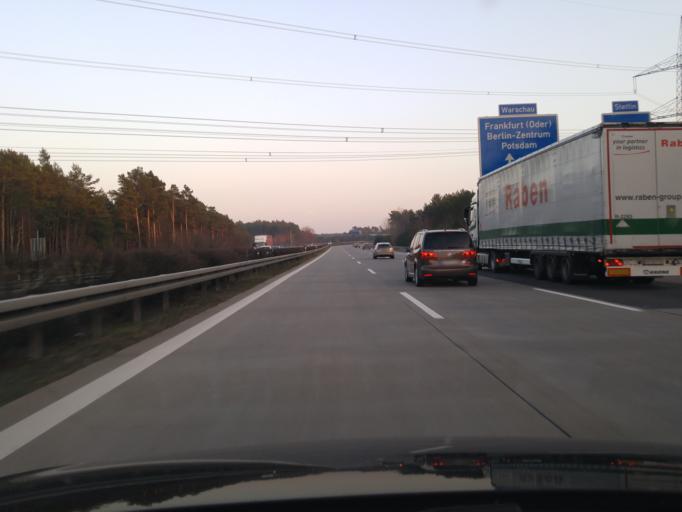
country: DE
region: Brandenburg
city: Gross Kreutz
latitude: 52.3381
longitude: 12.8015
